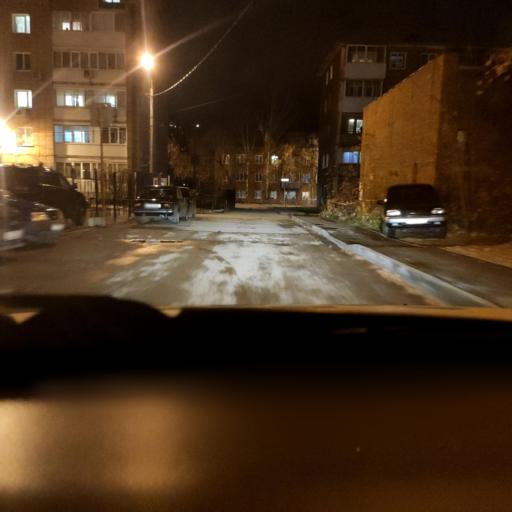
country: RU
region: Perm
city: Perm
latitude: 57.9790
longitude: 56.2044
